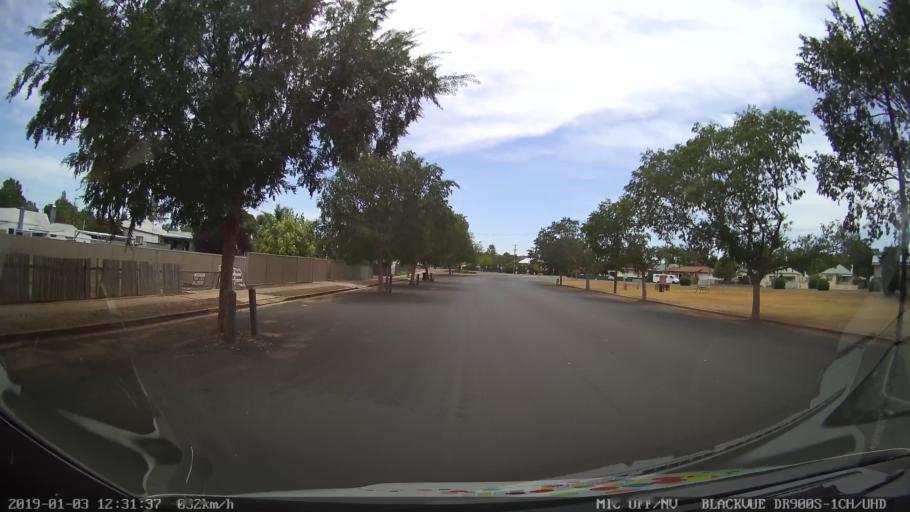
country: AU
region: New South Wales
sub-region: Weddin
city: Grenfell
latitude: -33.8939
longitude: 148.1638
